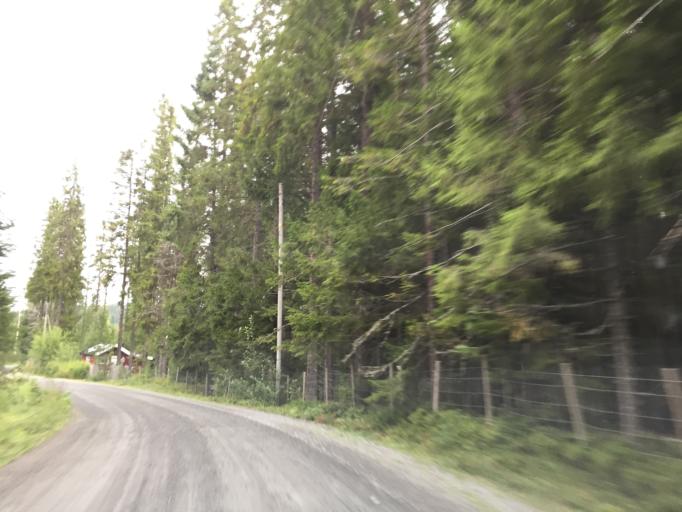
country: NO
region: Akershus
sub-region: Baerum
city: Lysaker
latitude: 60.0183
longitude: 10.5636
